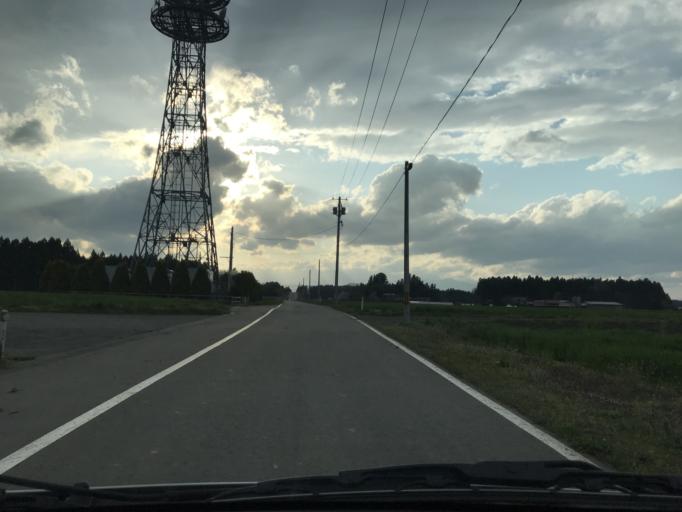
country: JP
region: Iwate
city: Mizusawa
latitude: 39.0990
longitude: 141.1238
